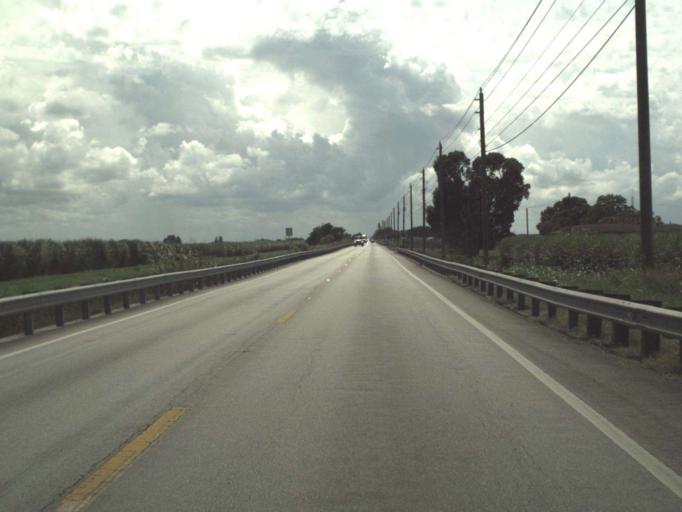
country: US
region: Florida
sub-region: Palm Beach County
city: Pahokee
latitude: 26.8037
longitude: -80.6534
